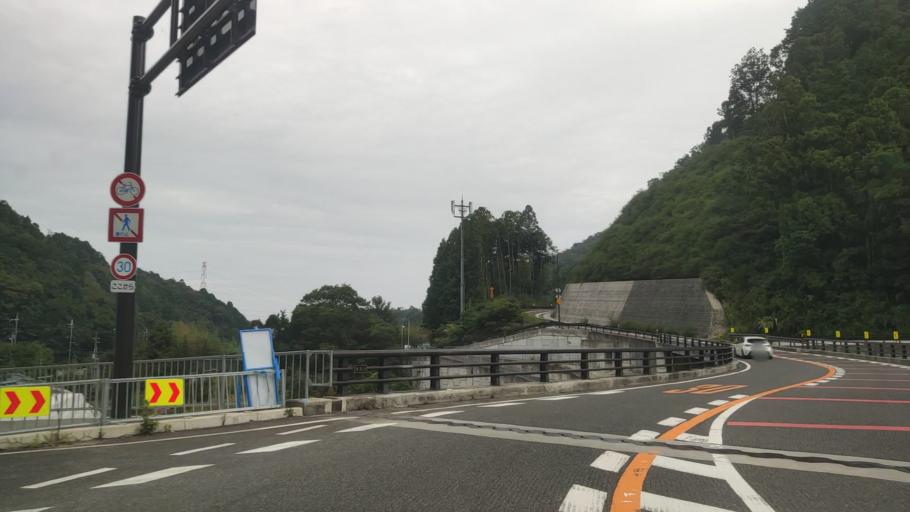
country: JP
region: Wakayama
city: Hashimoto
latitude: 34.3938
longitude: 135.5957
